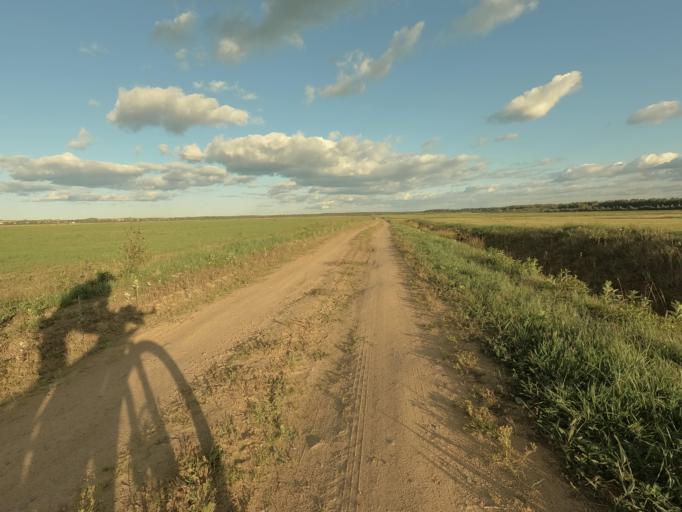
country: RU
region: Leningrad
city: Imeni Sverdlova
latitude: 59.8645
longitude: 30.7393
